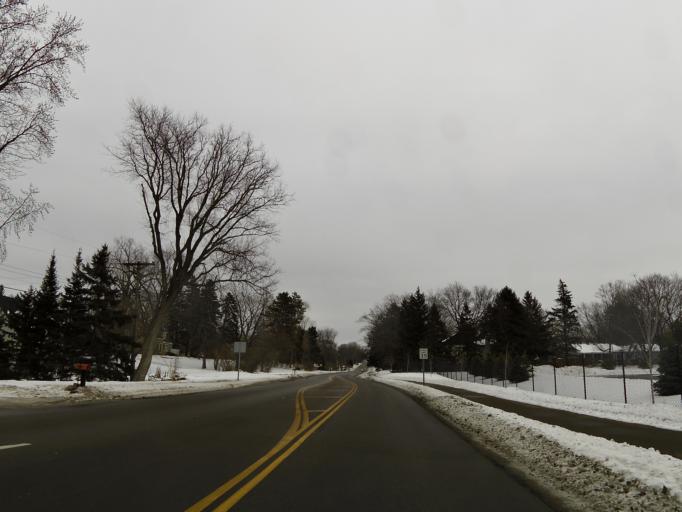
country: US
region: Minnesota
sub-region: Ramsey County
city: Little Canada
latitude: 45.0081
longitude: -93.0558
